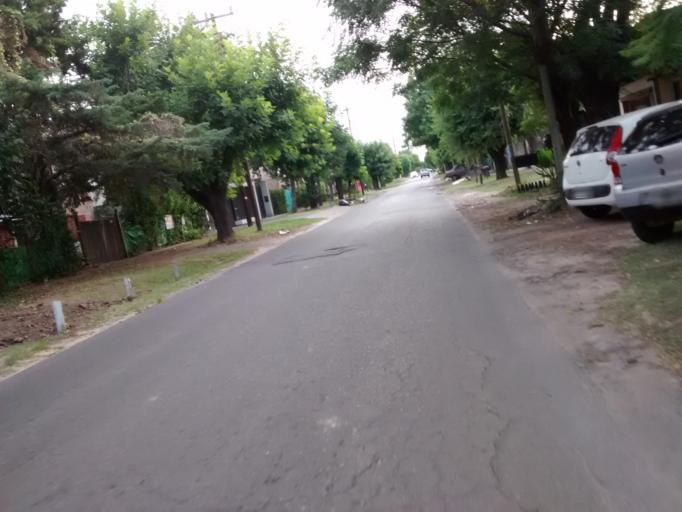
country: AR
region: Buenos Aires
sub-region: Partido de La Plata
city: La Plata
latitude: -34.8685
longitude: -58.0555
